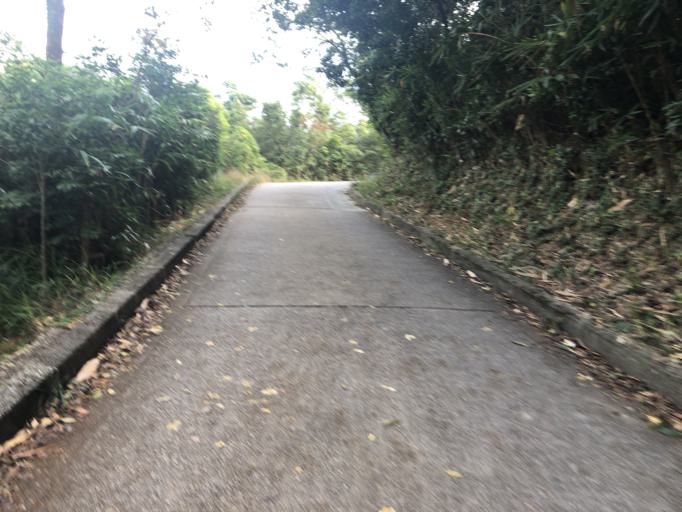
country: HK
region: Wanchai
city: Wan Chai
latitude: 22.2751
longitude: 114.2104
